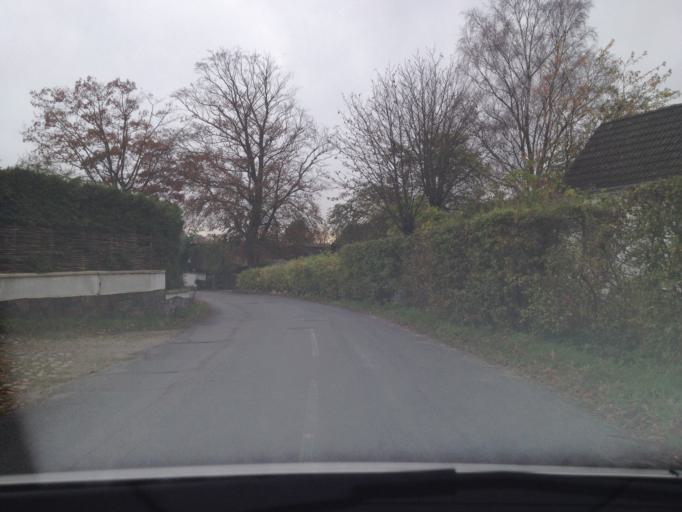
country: DK
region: Capital Region
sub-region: Hillerod Kommune
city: Nodebo
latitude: 55.9712
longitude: 12.3726
